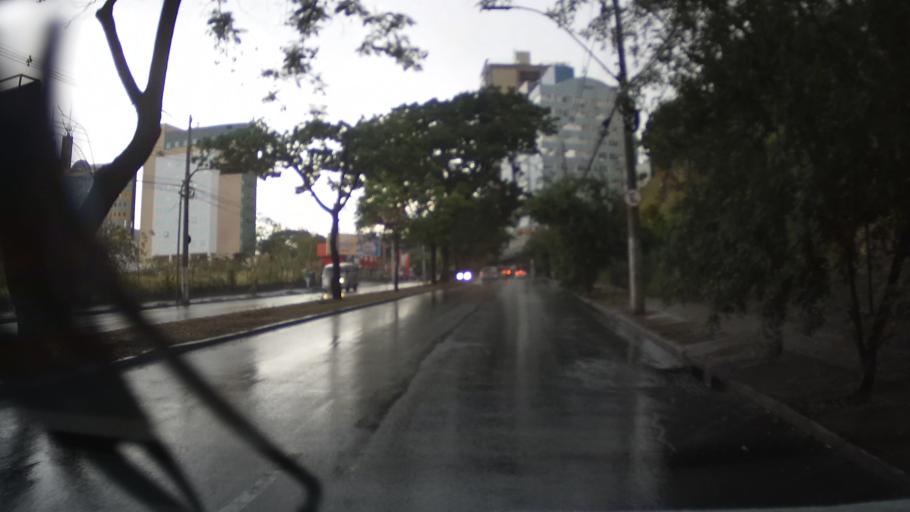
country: BR
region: Minas Gerais
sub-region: Belo Horizonte
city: Belo Horizonte
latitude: -19.9422
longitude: -43.9544
